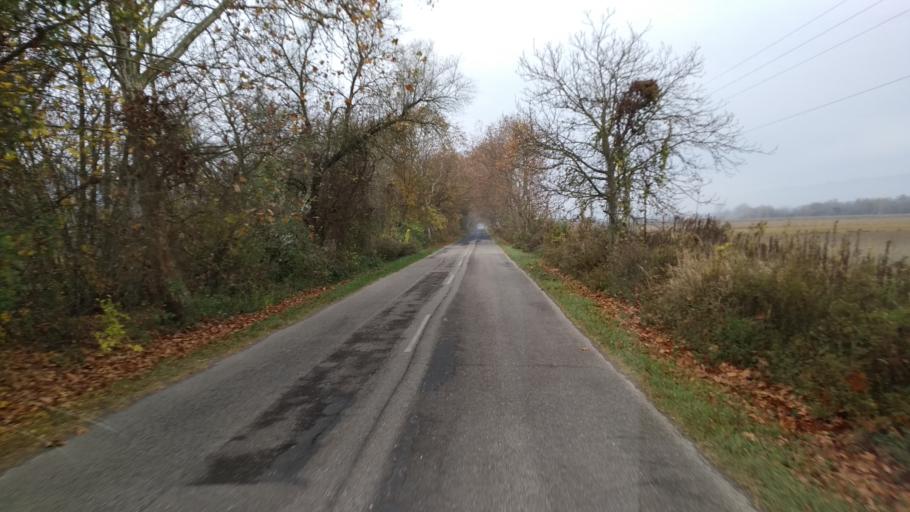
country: HU
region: Pest
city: Dunabogdany
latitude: 47.8023
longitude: 19.0333
